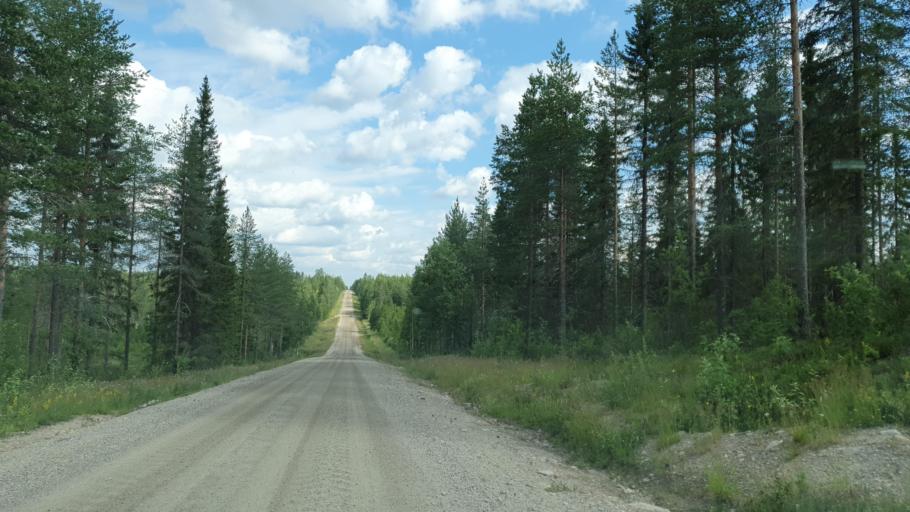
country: FI
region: Kainuu
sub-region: Kehys-Kainuu
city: Kuhmo
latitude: 64.4830
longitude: 29.5921
